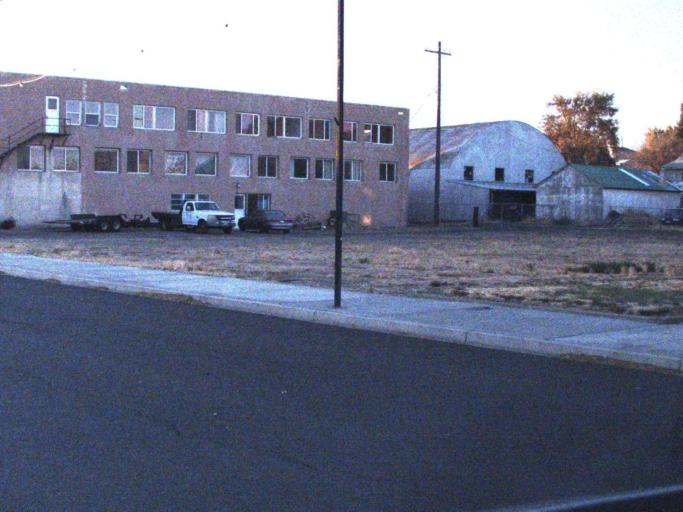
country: US
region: Washington
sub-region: Adams County
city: Ritzville
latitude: 46.9718
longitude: -118.6143
